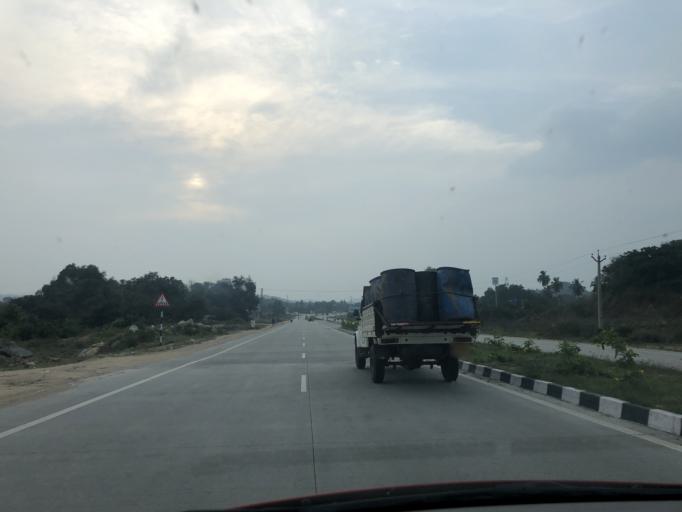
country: IN
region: Andhra Pradesh
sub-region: Chittoor
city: Chittoor
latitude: 13.1972
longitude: 78.9951
